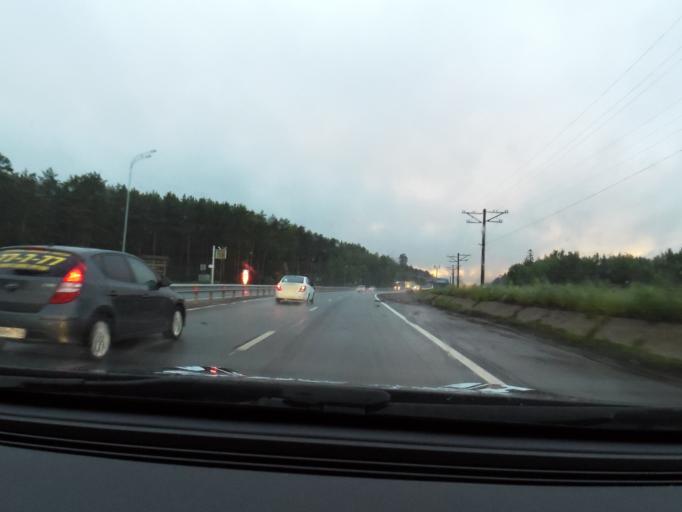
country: RU
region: Tatarstan
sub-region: Tukayevskiy Rayon
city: Naberezhnyye Chelny
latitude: 55.7225
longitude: 52.2601
